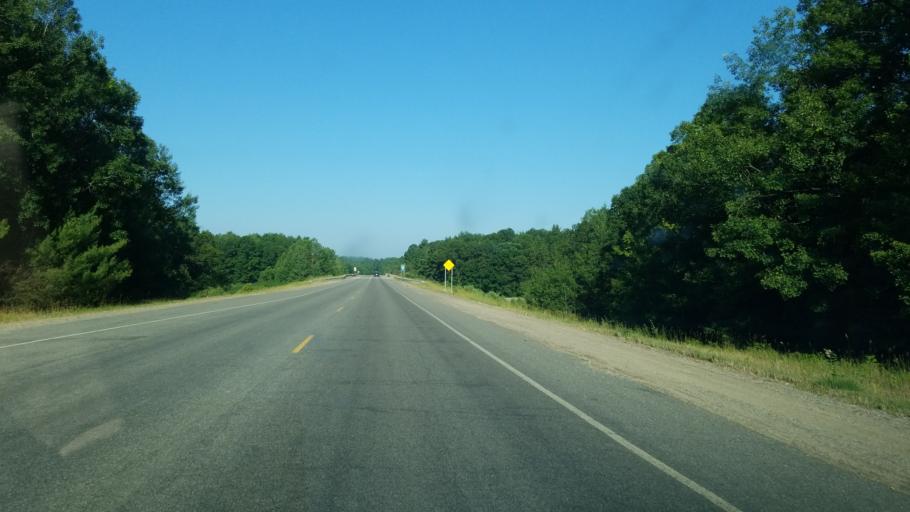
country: US
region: Michigan
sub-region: Montcalm County
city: Howard City
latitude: 43.4898
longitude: -85.4811
